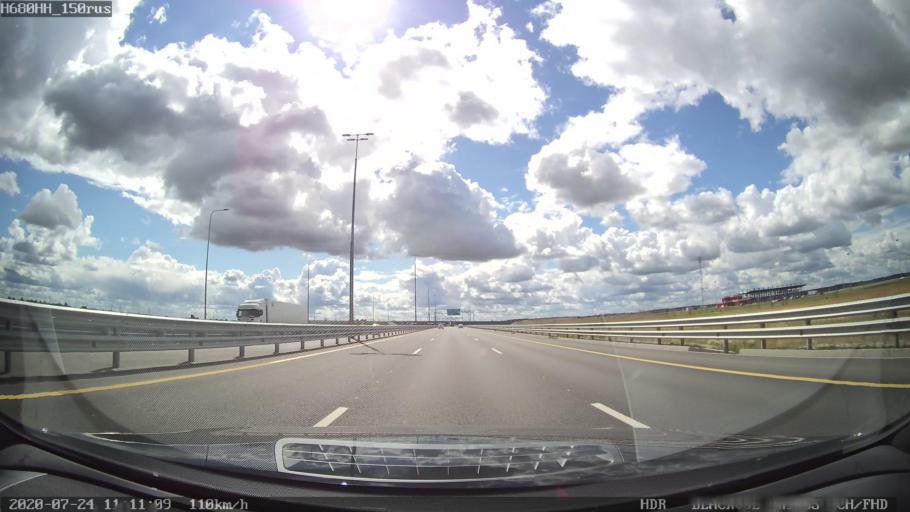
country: RU
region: St.-Petersburg
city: Tyarlevo
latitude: 59.7271
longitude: 30.5115
